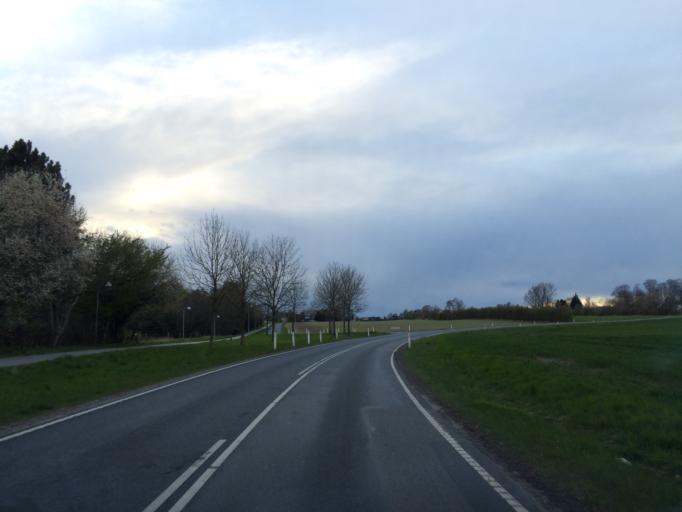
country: DK
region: South Denmark
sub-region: Odense Kommune
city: Bellinge
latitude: 55.3453
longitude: 10.2804
